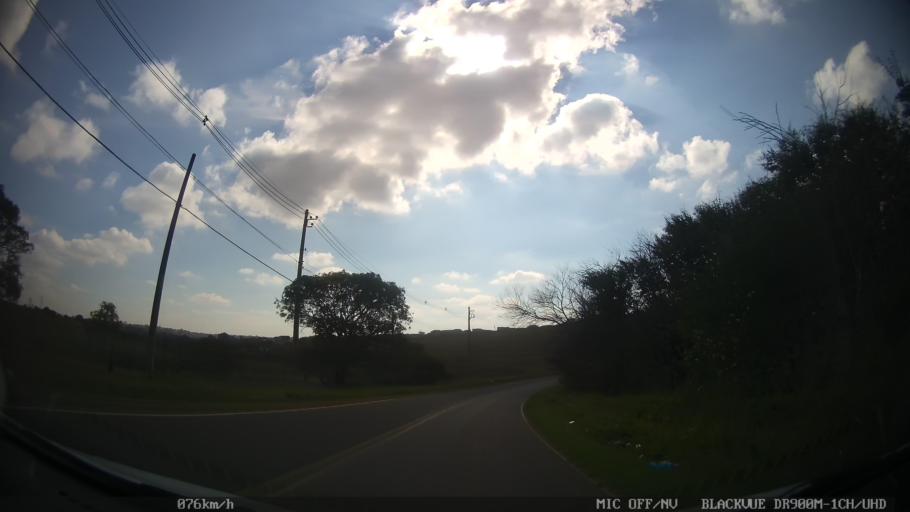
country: BR
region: Sao Paulo
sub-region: Indaiatuba
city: Indaiatuba
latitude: -22.9819
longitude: -47.1772
